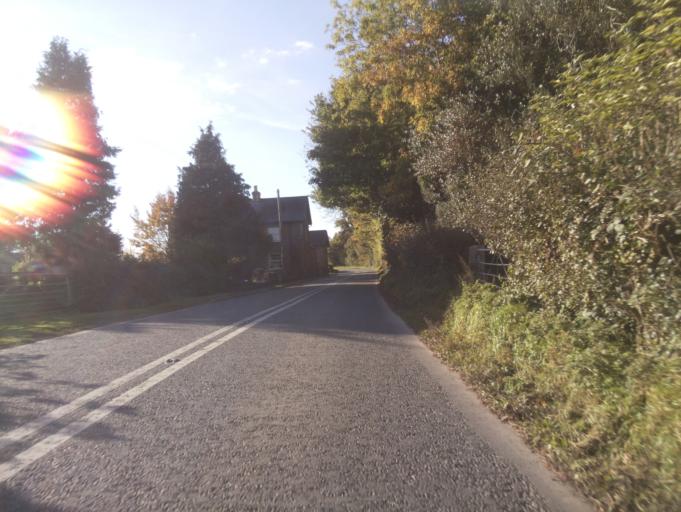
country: GB
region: England
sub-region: Herefordshire
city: Dorstone
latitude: 52.1170
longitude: -3.0214
